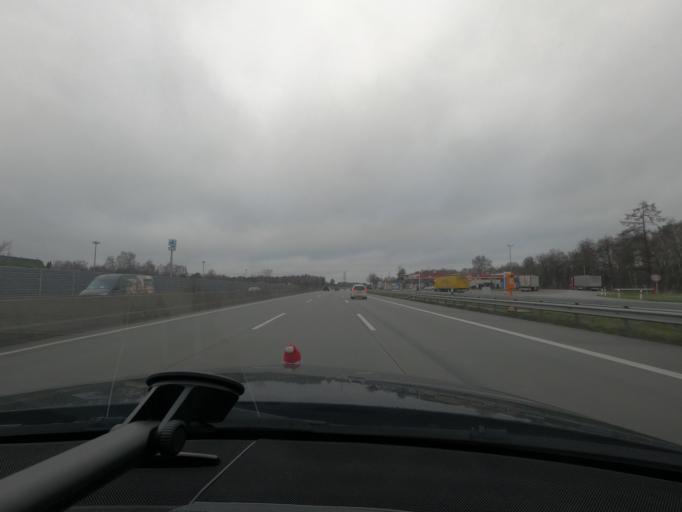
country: DE
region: Schleswig-Holstein
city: Quickborn
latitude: 53.7156
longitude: 9.9389
